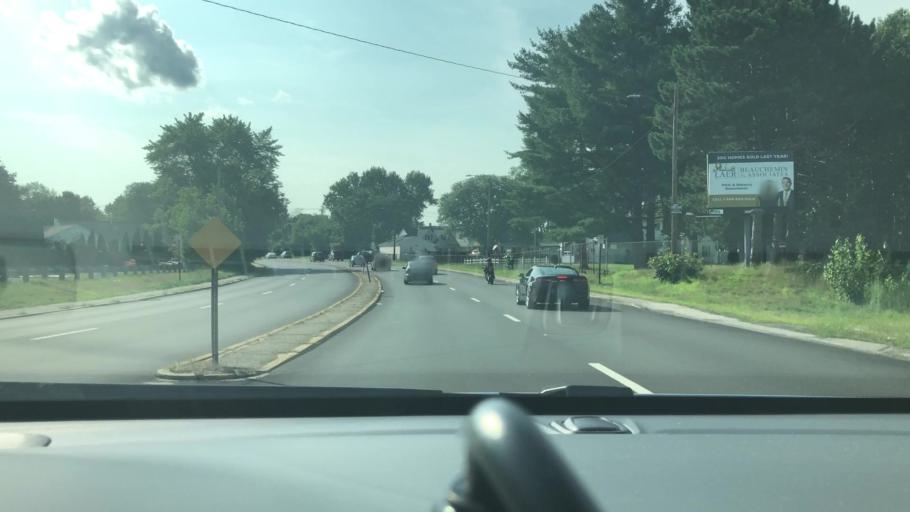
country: US
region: New Hampshire
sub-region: Hillsborough County
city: Manchester
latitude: 42.9733
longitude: -71.4590
